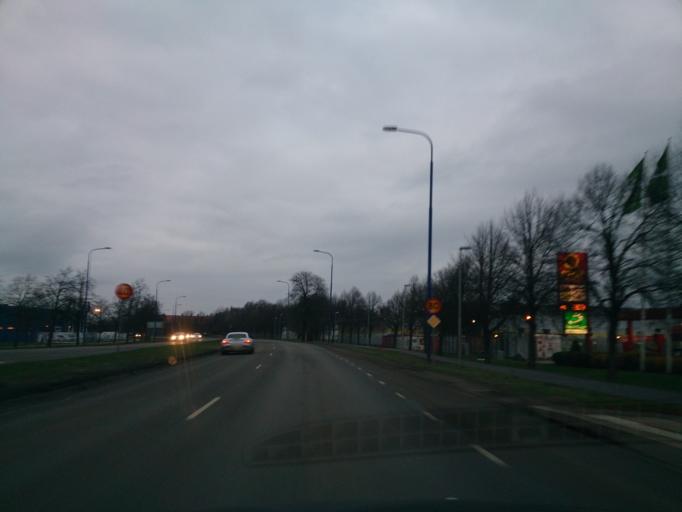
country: SE
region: OEstergoetland
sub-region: Norrkopings Kommun
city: Norrkoping
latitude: 58.6025
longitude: 16.1866
